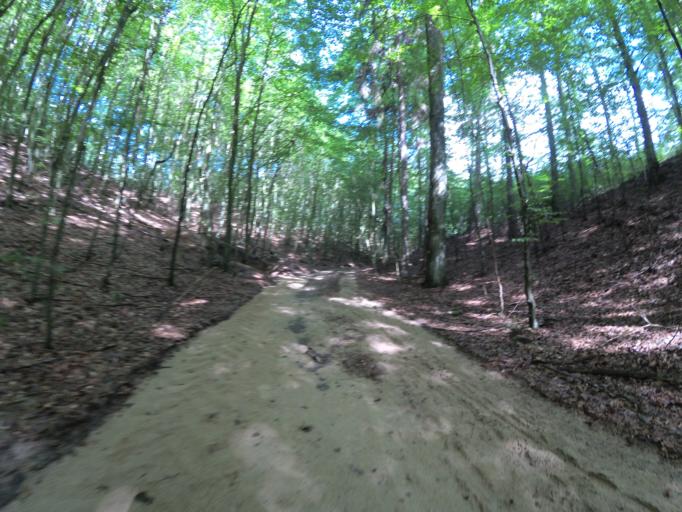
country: PL
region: Pomeranian Voivodeship
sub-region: Gdynia
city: Wielki Kack
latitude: 54.5106
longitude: 18.4502
